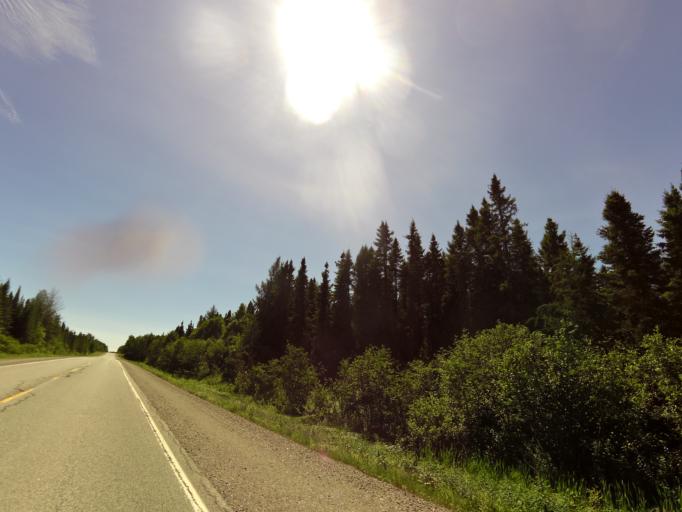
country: CA
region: Quebec
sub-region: Nord-du-Quebec
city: Lebel-sur-Quevillon
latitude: 48.8285
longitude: -77.1176
